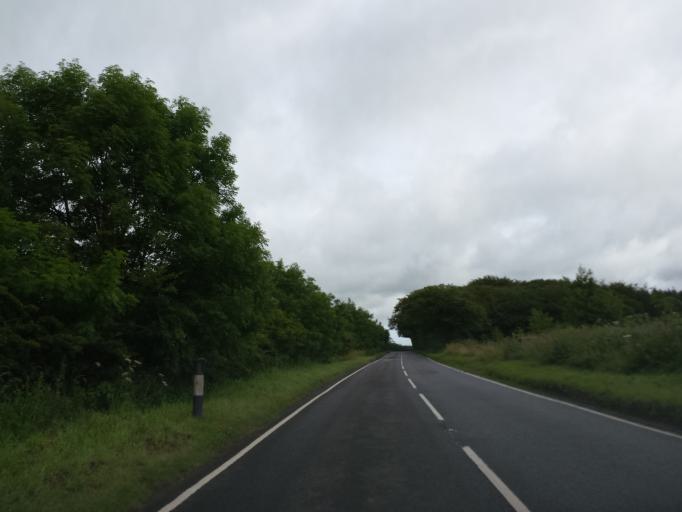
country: GB
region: Scotland
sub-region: Fife
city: Strathkinness
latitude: 56.2757
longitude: -2.8477
